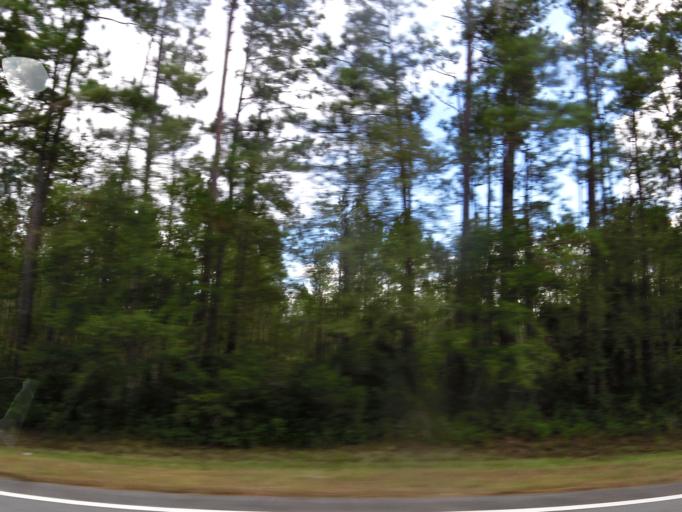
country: US
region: Georgia
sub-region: Brantley County
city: Nahunta
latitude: 31.0917
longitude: -82.0073
